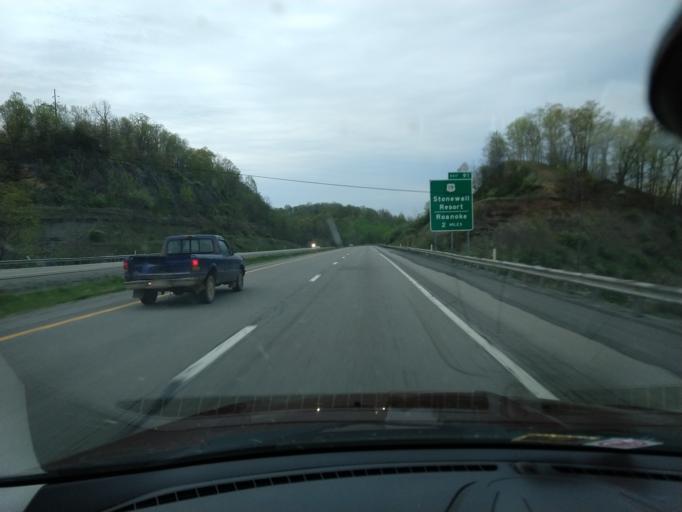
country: US
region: West Virginia
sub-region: Lewis County
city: Weston
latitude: 38.9448
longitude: -80.5387
